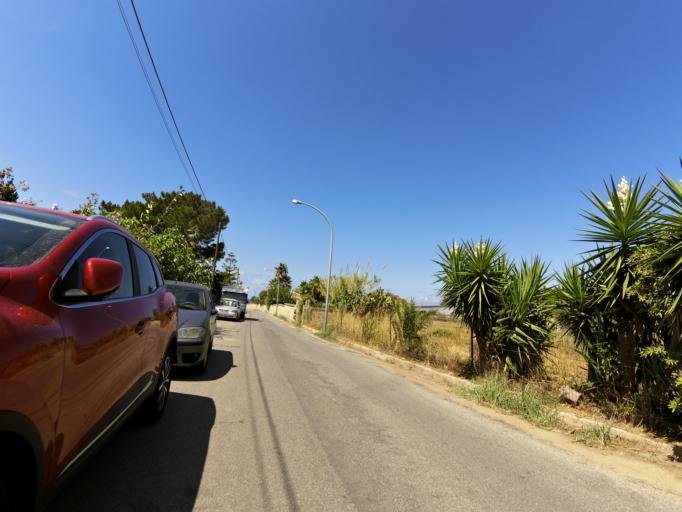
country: IT
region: Calabria
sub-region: Provincia di Vibo-Valentia
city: Santa Domenica
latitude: 38.6694
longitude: 15.8714
